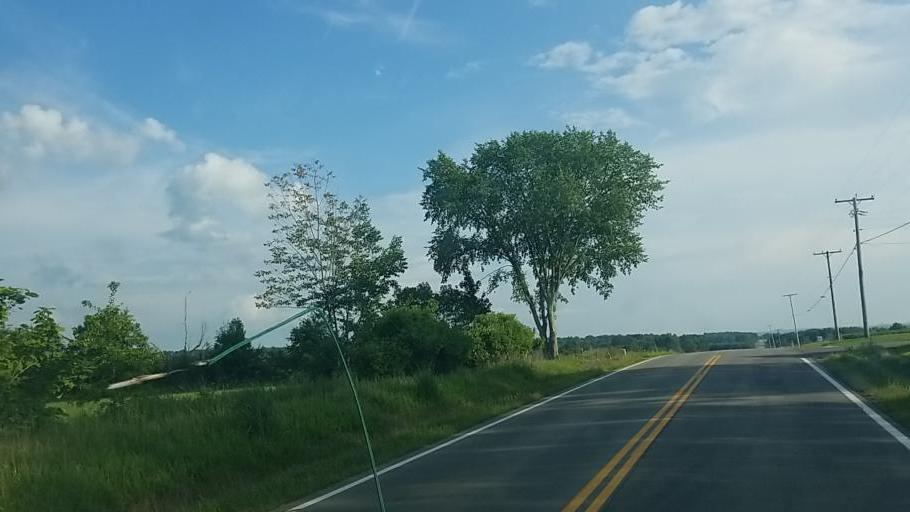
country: US
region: Ohio
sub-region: Ashland County
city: Ashland
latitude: 40.8646
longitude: -82.2120
